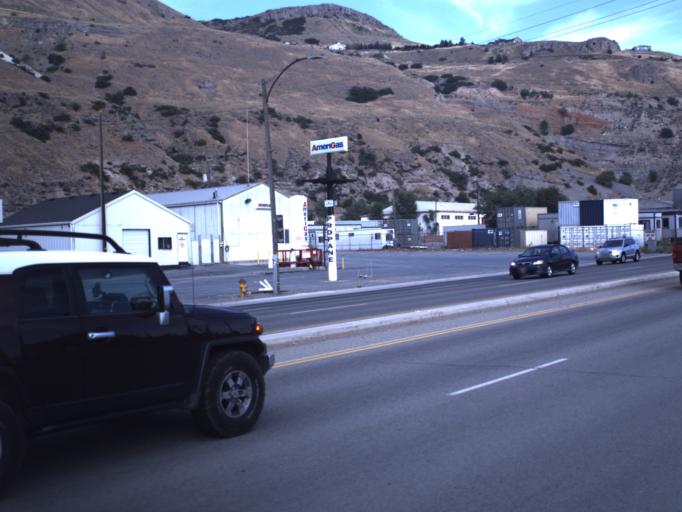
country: US
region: Utah
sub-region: Salt Lake County
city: Salt Lake City
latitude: 40.7961
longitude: -111.9059
